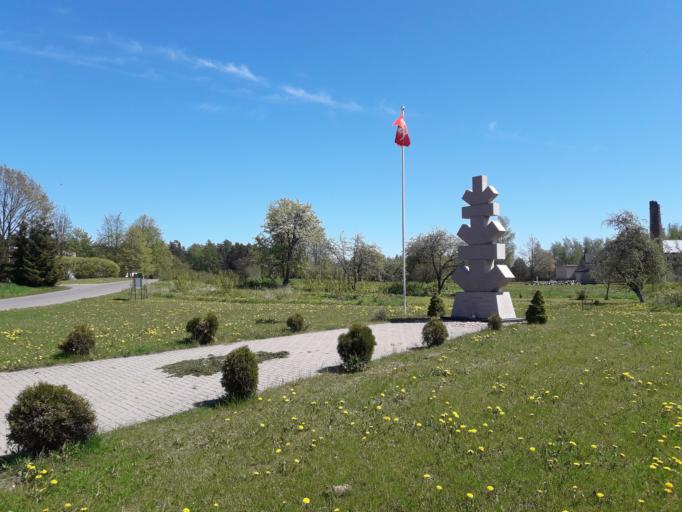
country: LT
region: Panevezys
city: Rokiskis
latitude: 55.9075
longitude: 25.5628
